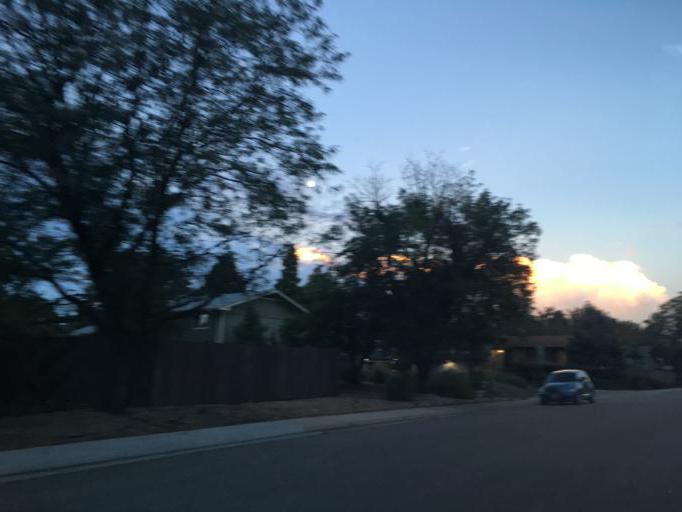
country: US
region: Colorado
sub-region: Adams County
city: Aurora
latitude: 39.6877
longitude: -104.8498
